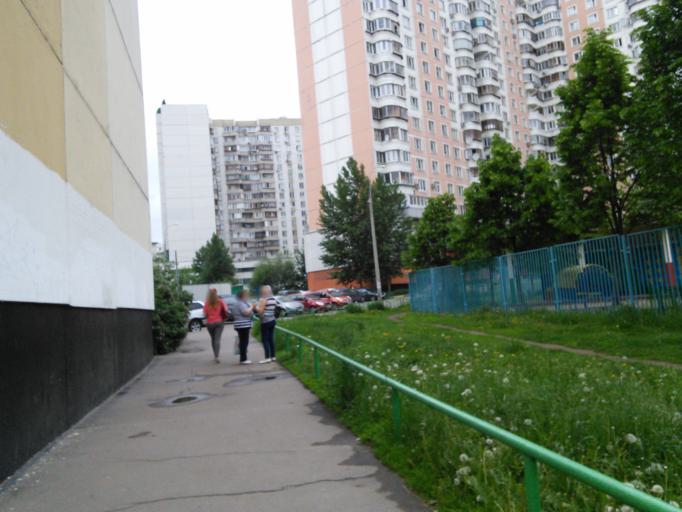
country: RU
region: Moscow
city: Lyublino
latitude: 55.6582
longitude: 37.7540
